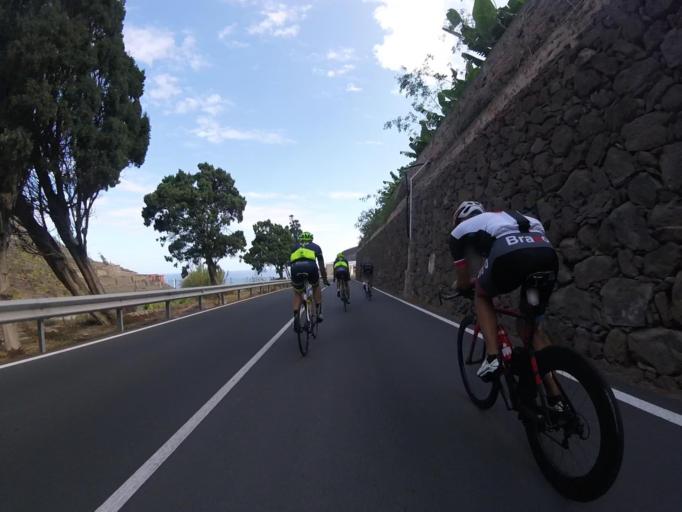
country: ES
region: Canary Islands
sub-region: Provincia de Las Palmas
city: Moya
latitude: 28.1391
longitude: -15.5898
